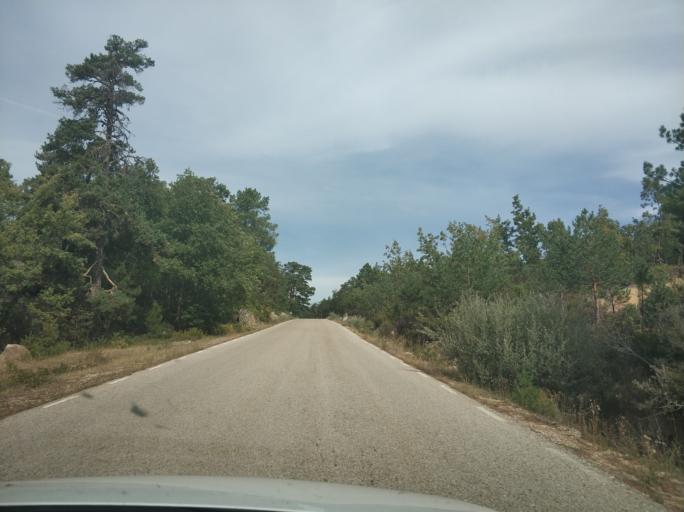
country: ES
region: Castille and Leon
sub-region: Provincia de Soria
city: Duruelo de la Sierra
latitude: 41.9108
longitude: -2.9474
